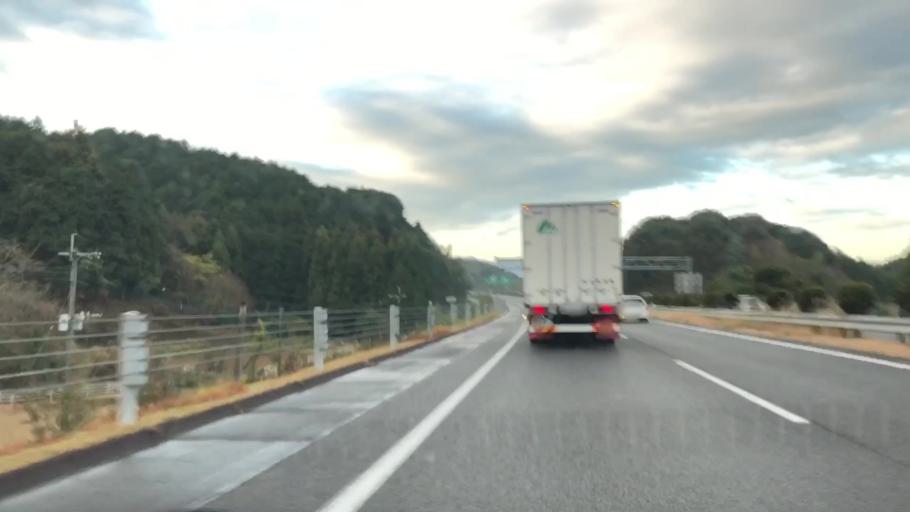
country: JP
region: Saga Prefecture
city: Takeocho-takeo
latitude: 33.1559
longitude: 130.0048
